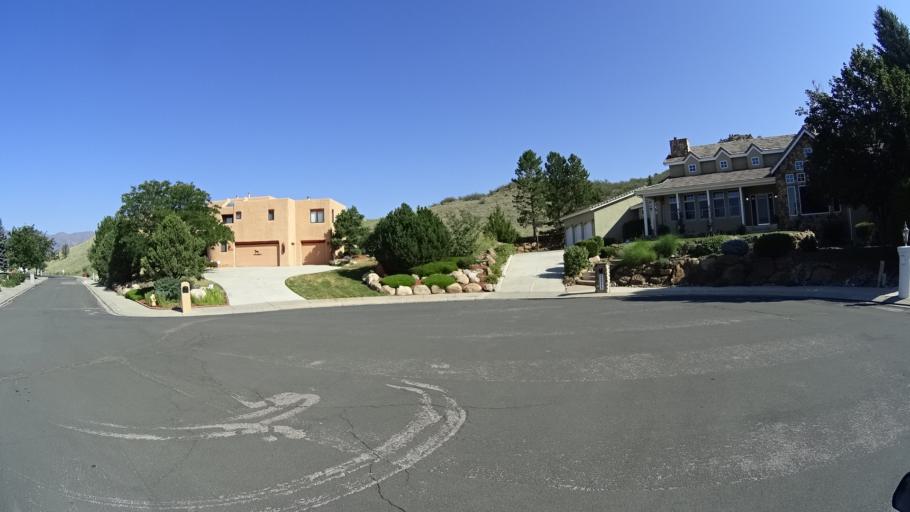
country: US
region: Colorado
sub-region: El Paso County
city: Colorado Springs
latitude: 38.8787
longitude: -104.7861
